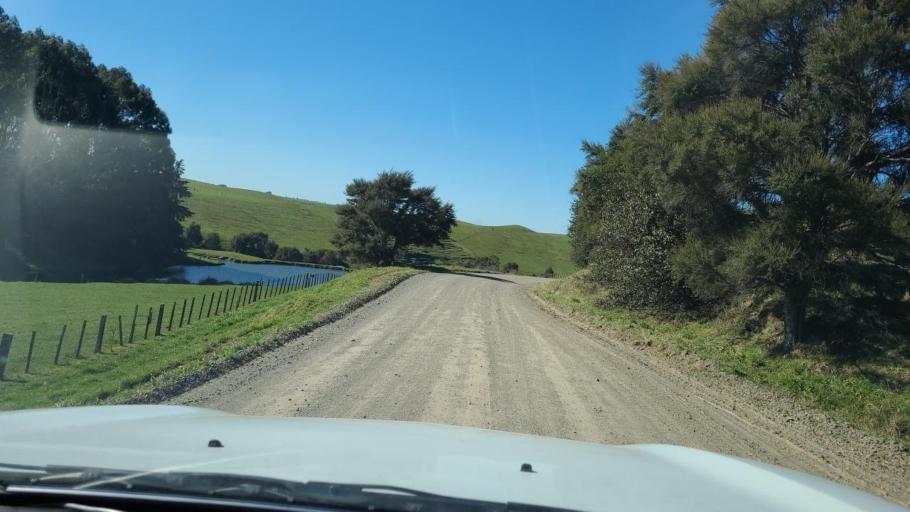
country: NZ
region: Hawke's Bay
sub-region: Napier City
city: Taradale
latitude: -39.4233
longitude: 176.5011
